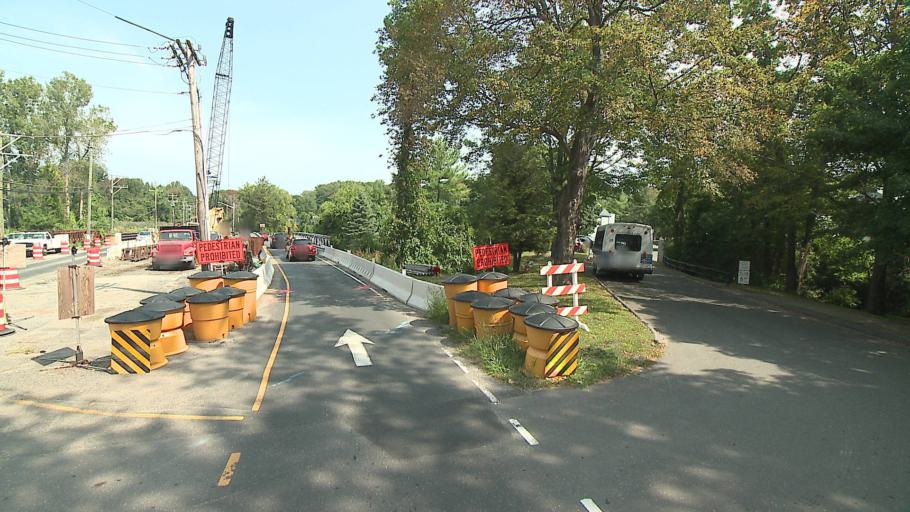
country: US
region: Connecticut
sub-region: Fairfield County
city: Ridgefield
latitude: 41.2972
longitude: -73.4924
